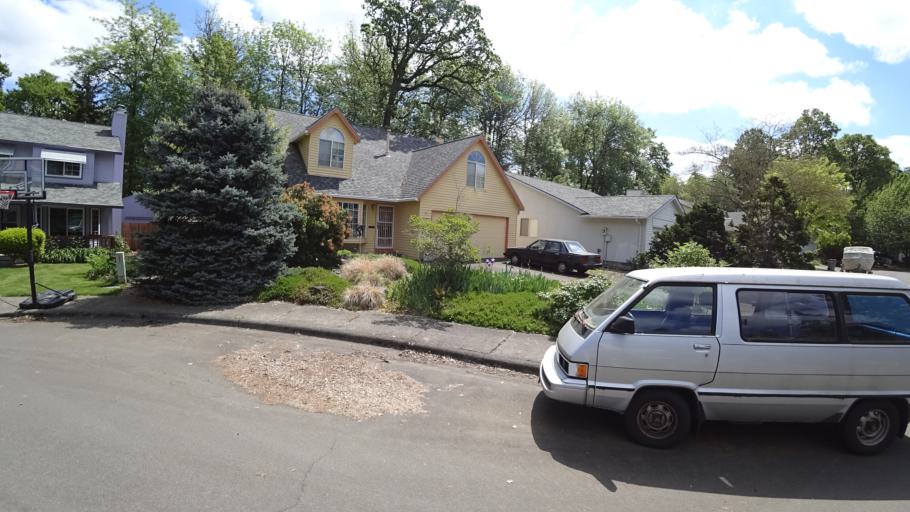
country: US
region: Oregon
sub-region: Washington County
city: Aloha
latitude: 45.5115
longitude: -122.8948
